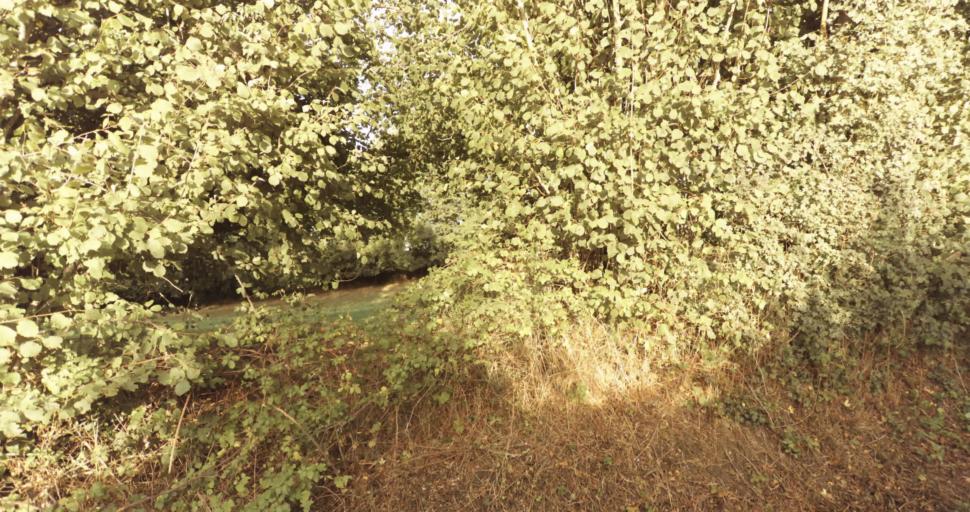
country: FR
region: Lower Normandy
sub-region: Departement de l'Orne
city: Sees
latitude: 48.6934
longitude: 0.2254
